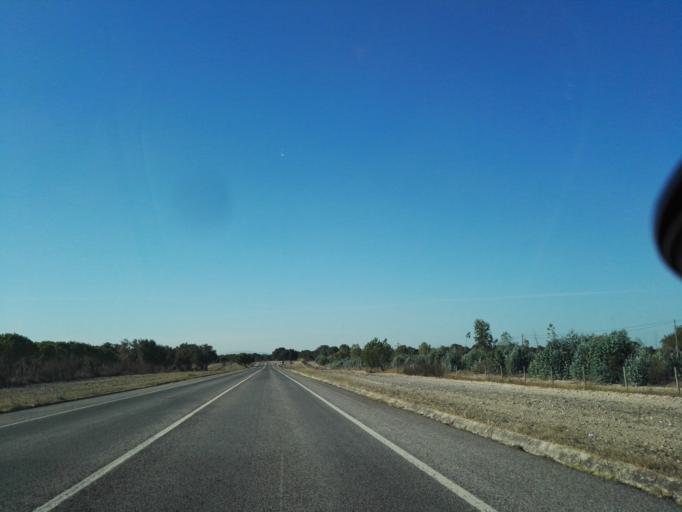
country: PT
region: Santarem
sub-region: Benavente
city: Poceirao
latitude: 38.8536
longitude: -8.7743
